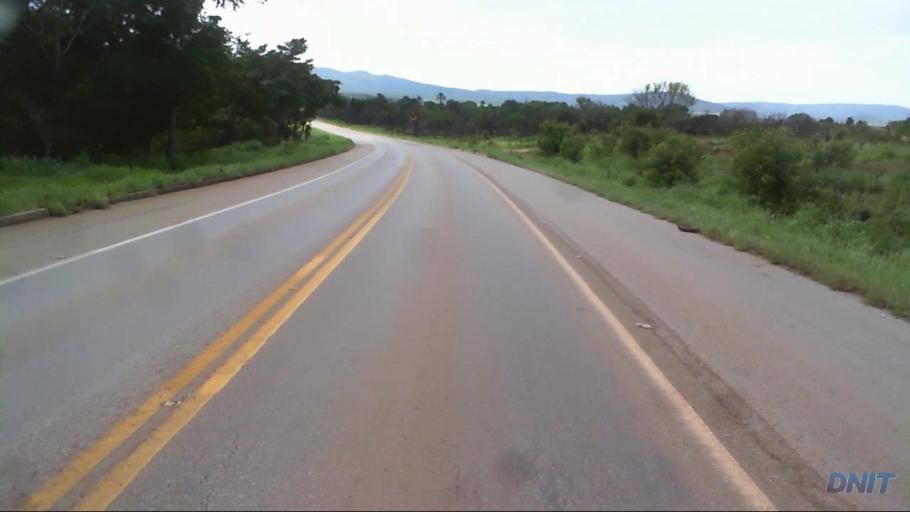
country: BR
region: Goias
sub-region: Barro Alto
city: Barro Alto
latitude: -15.1765
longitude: -48.7936
